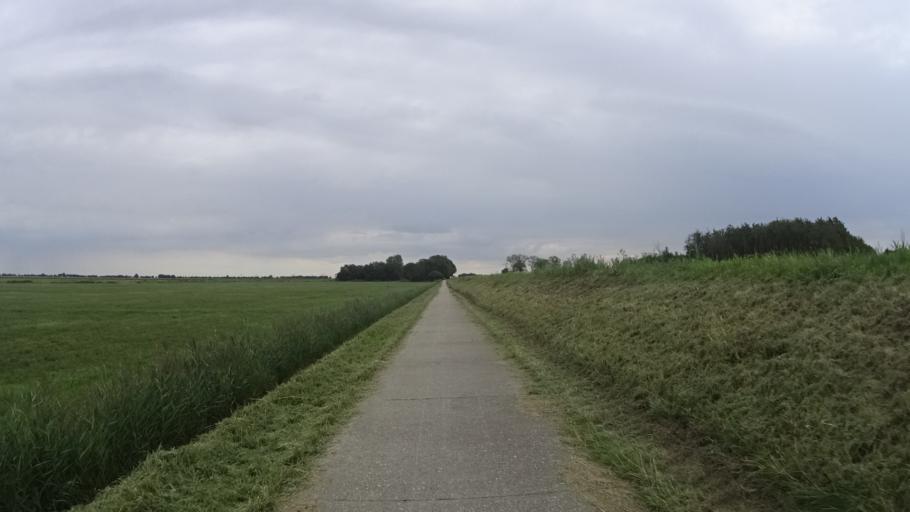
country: NL
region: Groningen
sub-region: Gemeente Haren
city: Haren
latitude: 53.2356
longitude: 6.6849
